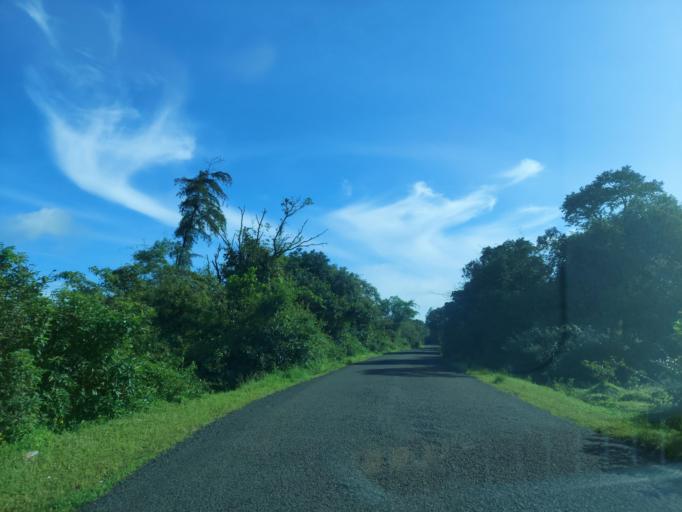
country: IN
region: Maharashtra
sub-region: Kolhapur
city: Ajra
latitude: 16.0179
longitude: 74.0515
